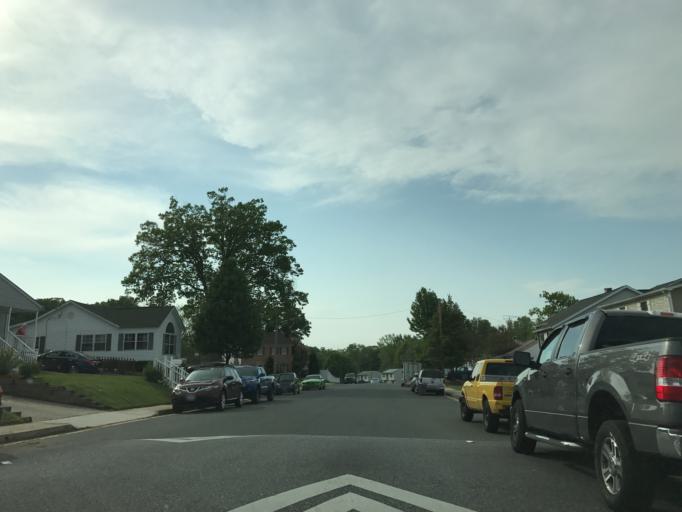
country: US
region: Maryland
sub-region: Baltimore County
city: Middle River
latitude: 39.3358
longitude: -76.4592
